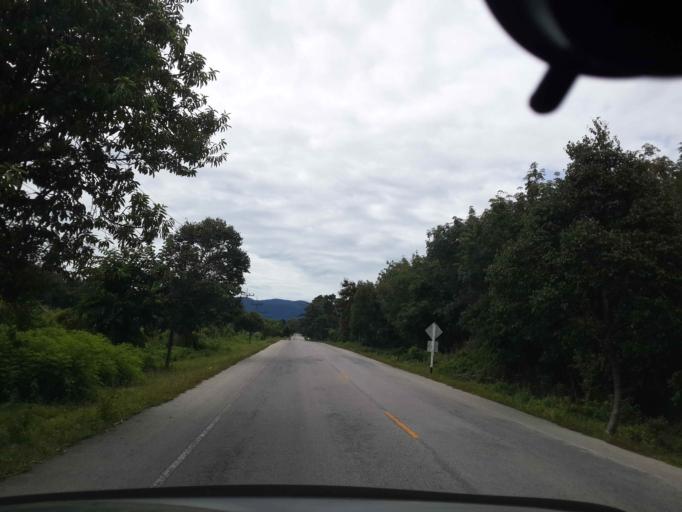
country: TH
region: Narathiwat
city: Rueso
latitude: 6.3795
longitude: 101.5255
